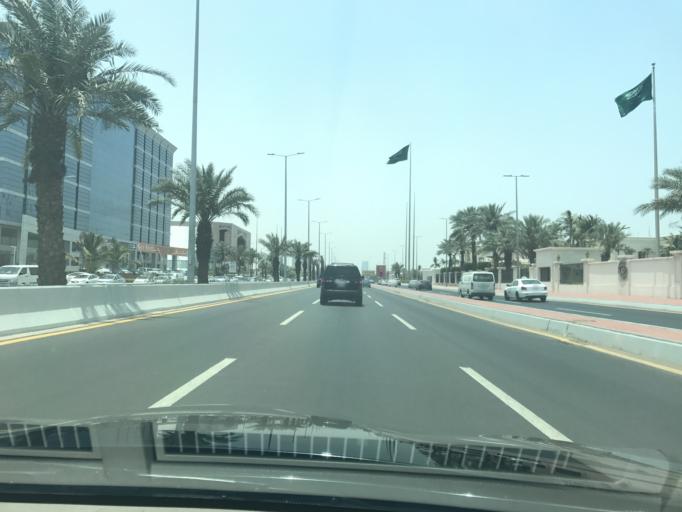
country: SA
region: Makkah
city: Jeddah
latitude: 21.5447
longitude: 39.1760
